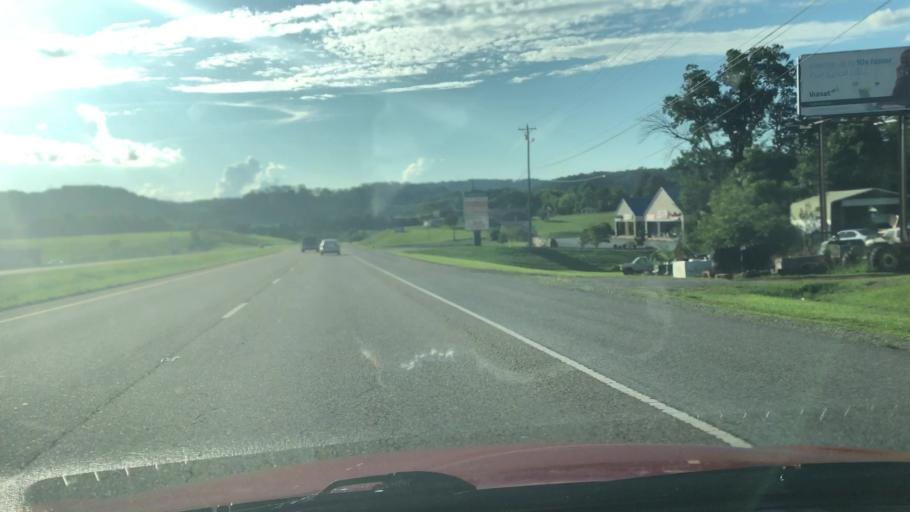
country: US
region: Tennessee
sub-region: Jefferson County
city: Dandridge
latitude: 36.0457
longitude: -83.4557
